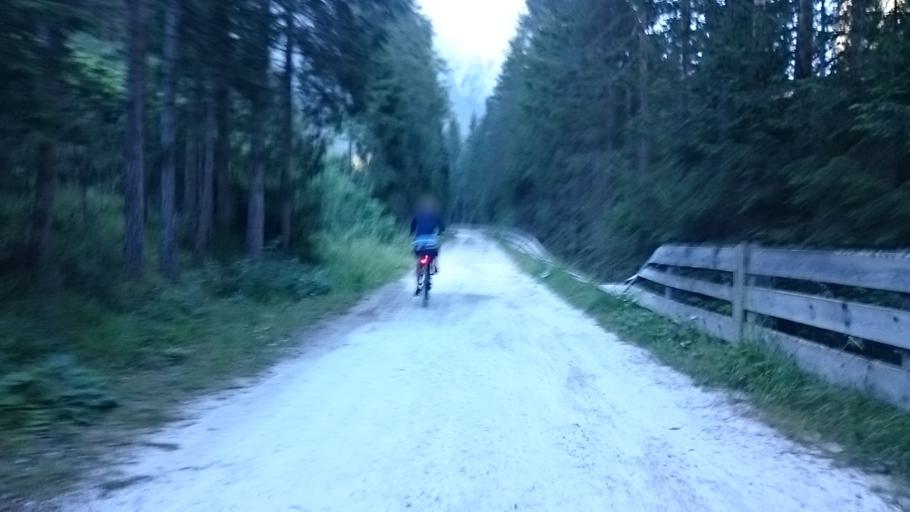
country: IT
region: Trentino-Alto Adige
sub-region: Bolzano
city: Dobbiaco
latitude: 46.6940
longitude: 12.2226
